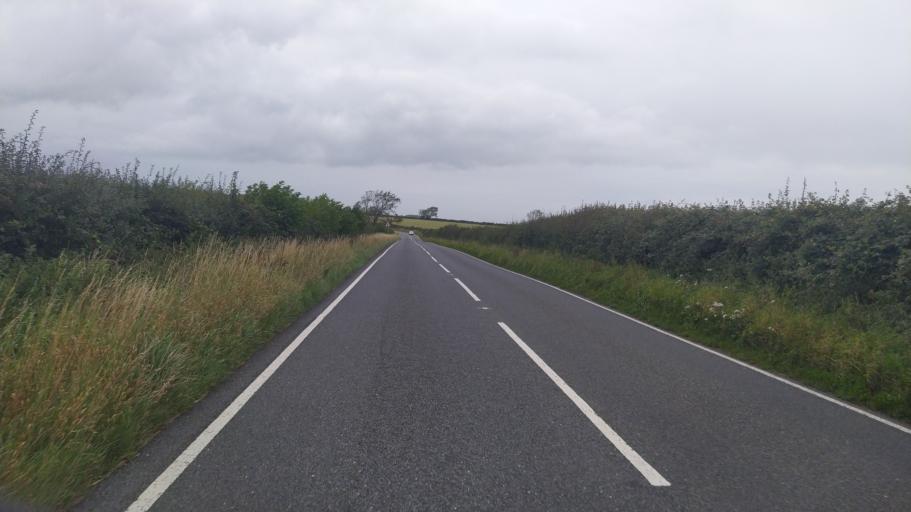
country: GB
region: England
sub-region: Dorset
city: Dorchester
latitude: 50.8153
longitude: -2.4557
